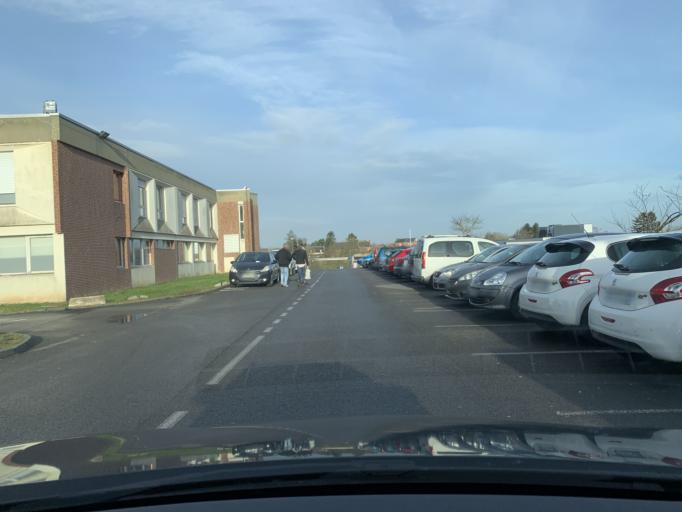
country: FR
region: Nord-Pas-de-Calais
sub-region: Departement du Nord
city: Cambrai
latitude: 50.1646
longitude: 3.2257
